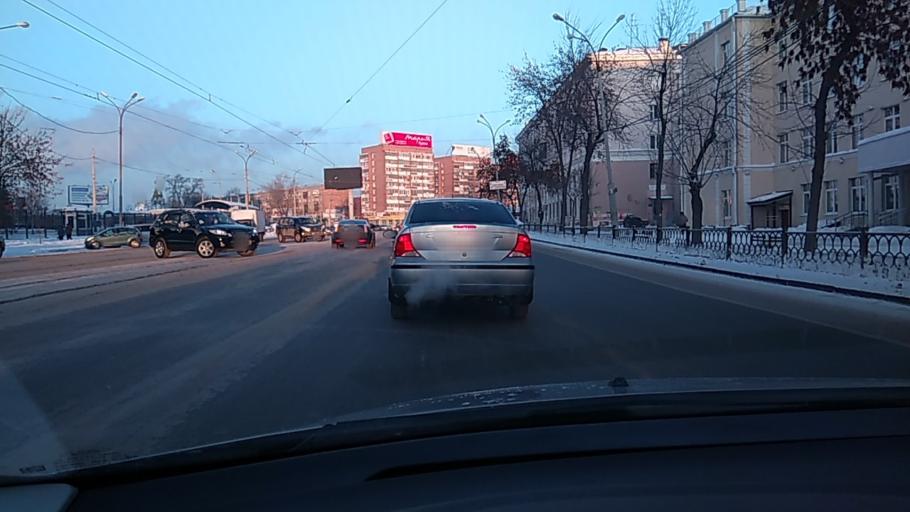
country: RU
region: Sverdlovsk
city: Yekaterinburg
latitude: 56.8546
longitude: 60.5991
